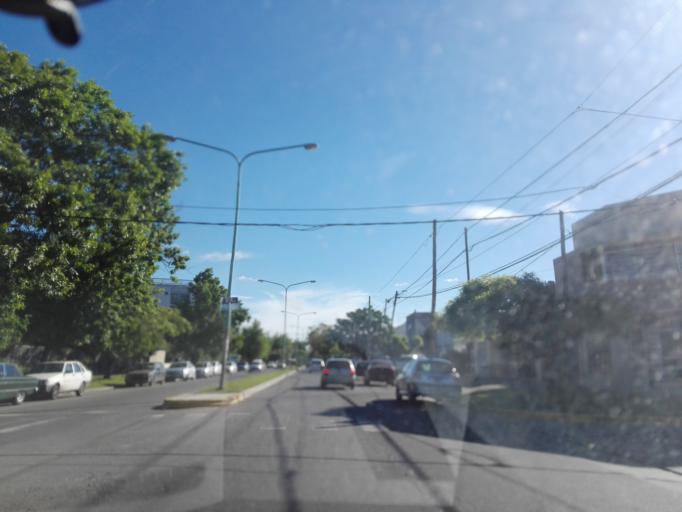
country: AR
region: Buenos Aires
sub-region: Partido de La Plata
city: La Plata
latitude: -34.8906
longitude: -58.0073
